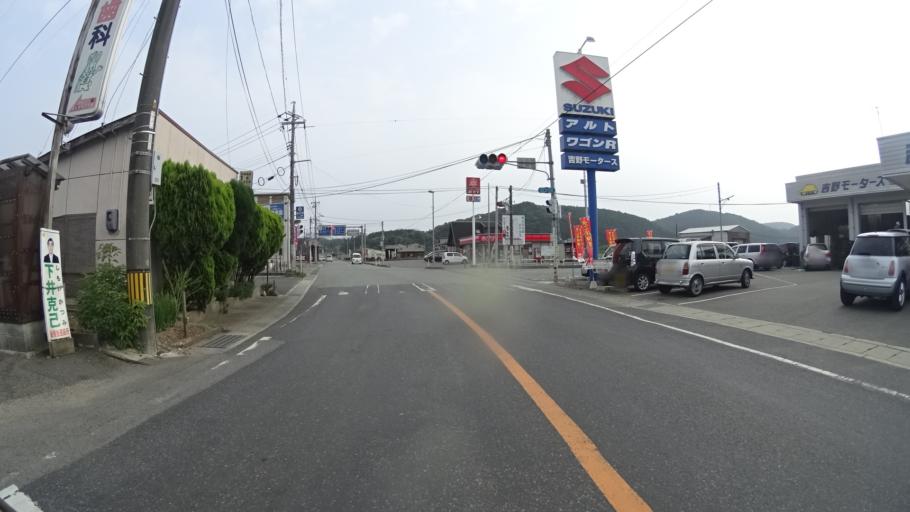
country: JP
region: Yamaguchi
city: Ogori-shimogo
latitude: 34.2142
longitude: 131.2907
